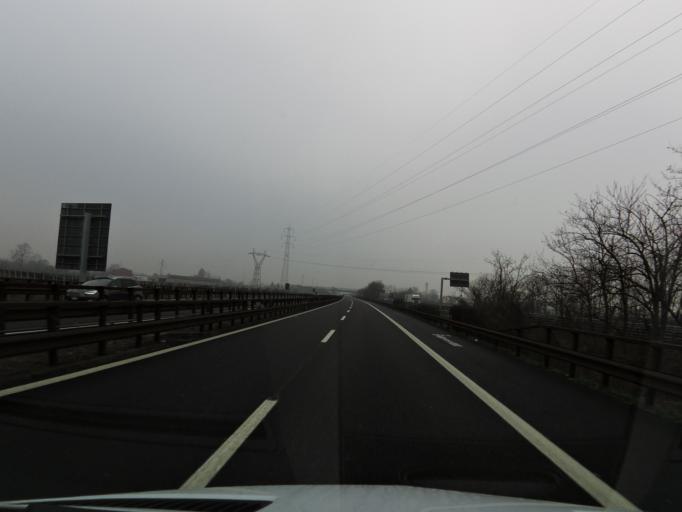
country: IT
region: Veneto
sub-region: Provincia di Verona
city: Bassone
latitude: 45.4365
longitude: 10.9029
